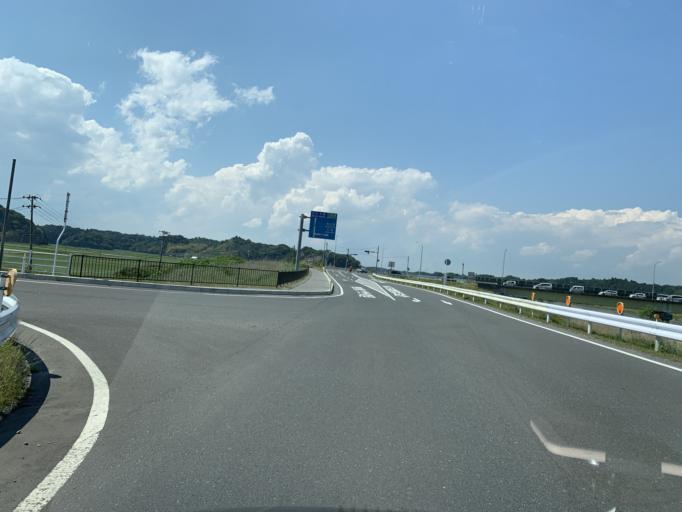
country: JP
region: Miyagi
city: Yamoto
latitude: 38.3944
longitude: 141.1561
